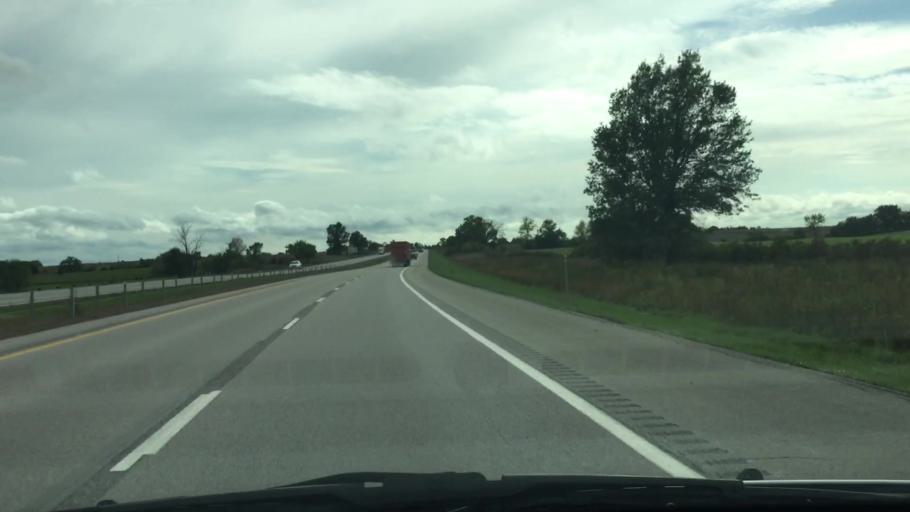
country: US
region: Iowa
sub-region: Clarke County
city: Osceola
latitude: 41.1615
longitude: -93.7848
